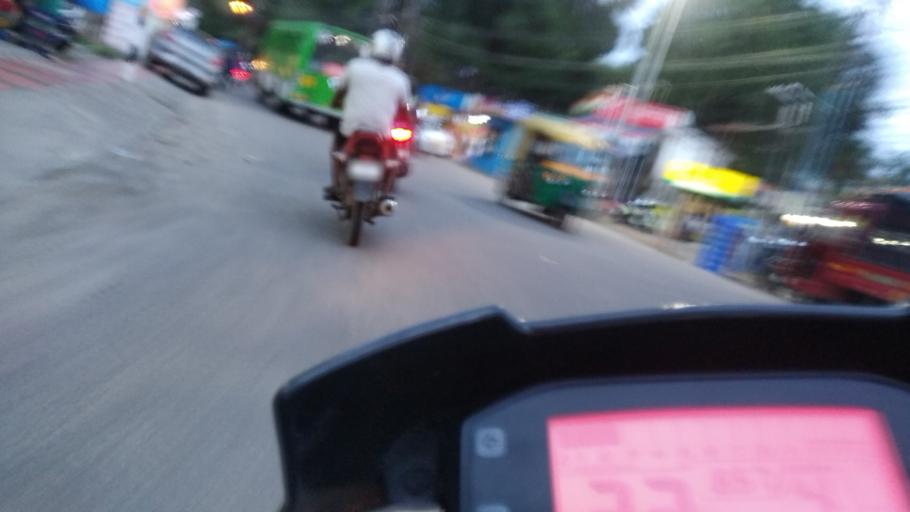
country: IN
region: Kerala
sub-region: Ernakulam
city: Elur
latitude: 10.0192
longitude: 76.2748
